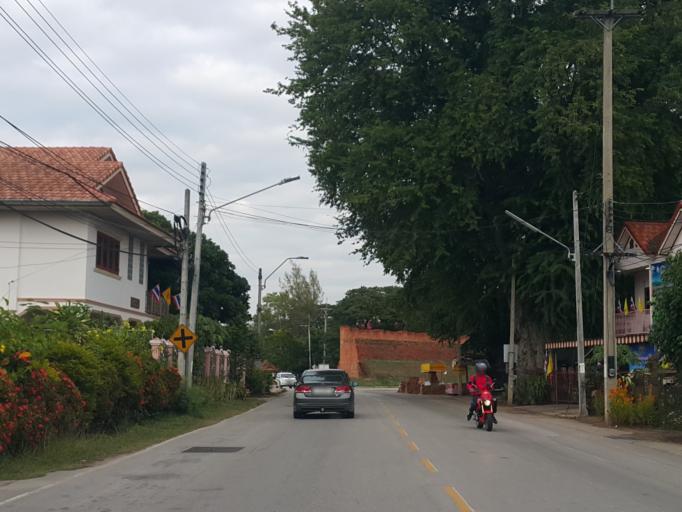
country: TH
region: Lampang
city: Lampang
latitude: 18.3067
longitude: 99.5113
